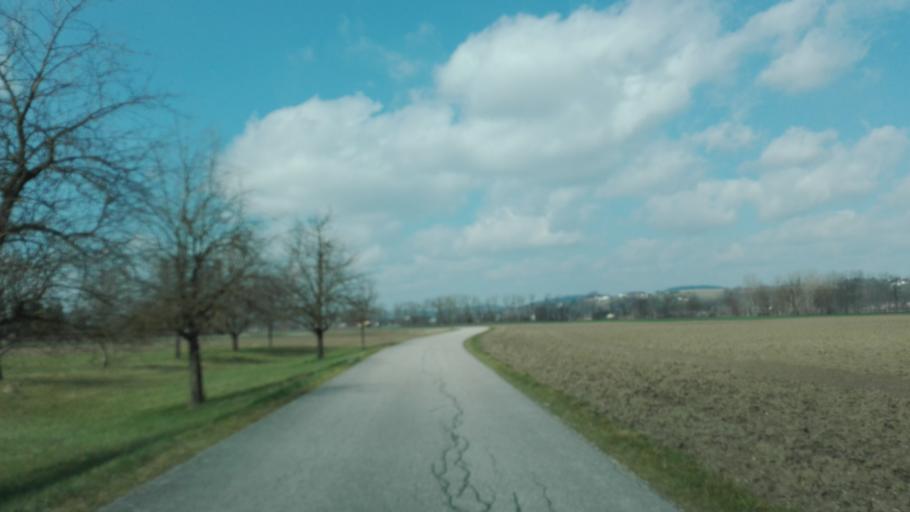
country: AT
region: Upper Austria
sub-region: Politischer Bezirk Urfahr-Umgebung
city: Walding
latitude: 48.3242
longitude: 14.1432
